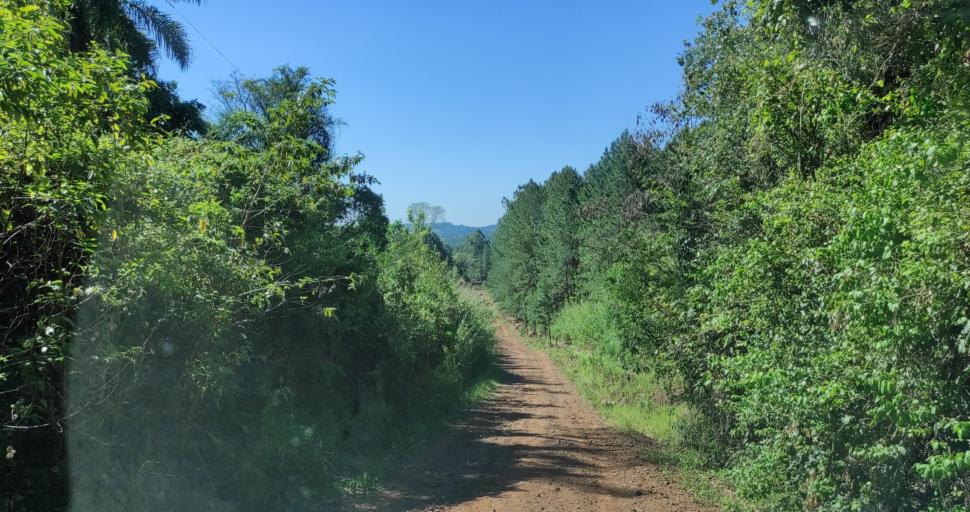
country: AR
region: Misiones
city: Capiovi
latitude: -26.9429
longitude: -55.0026
